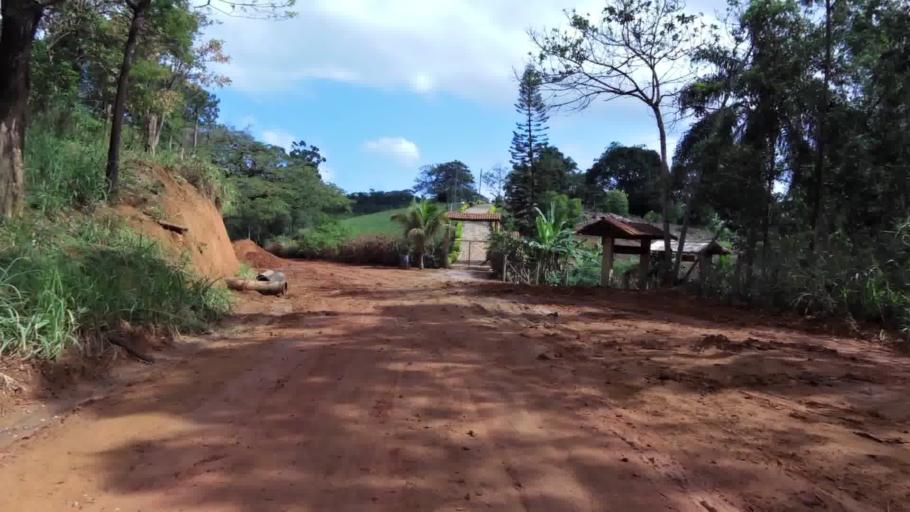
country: BR
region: Espirito Santo
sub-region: Piuma
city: Piuma
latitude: -20.8119
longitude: -40.6708
